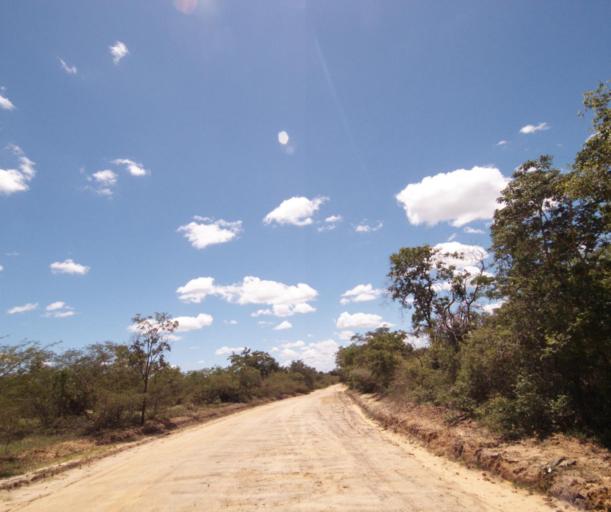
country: BR
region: Bahia
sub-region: Carinhanha
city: Carinhanha
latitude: -14.2101
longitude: -43.9782
